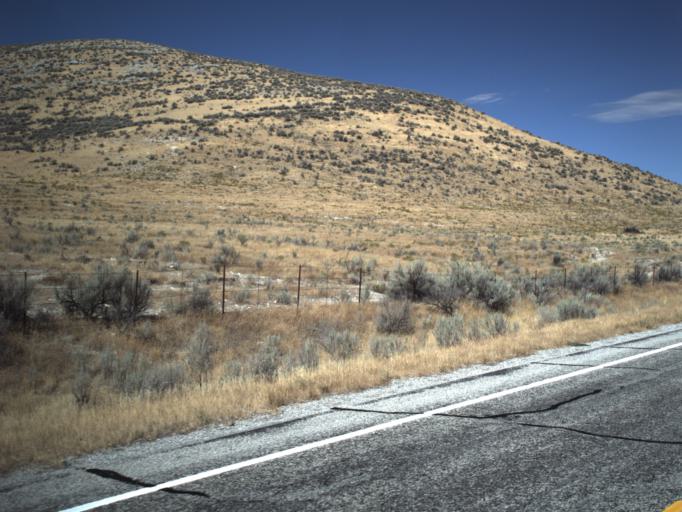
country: US
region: Utah
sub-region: Box Elder County
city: Tremonton
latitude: 41.7019
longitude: -112.4480
